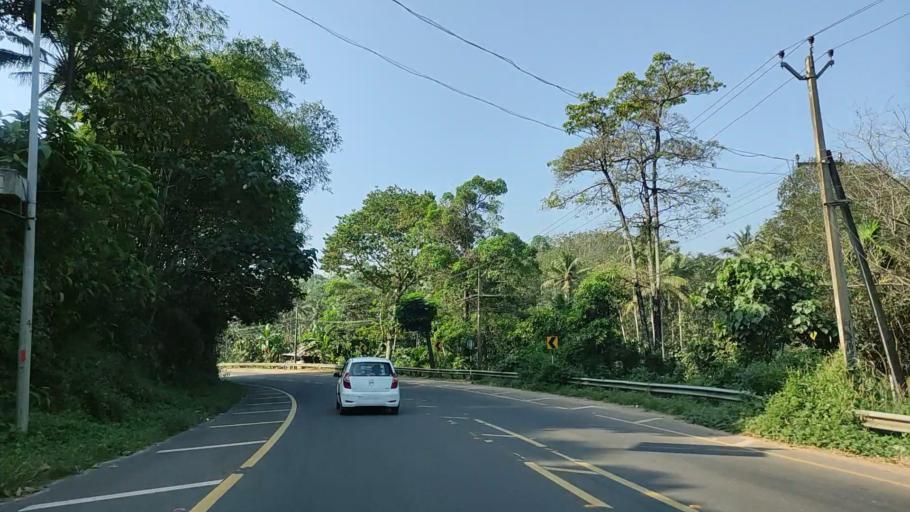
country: IN
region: Kerala
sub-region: Kollam
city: Punalur
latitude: 8.9078
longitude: 76.8546
